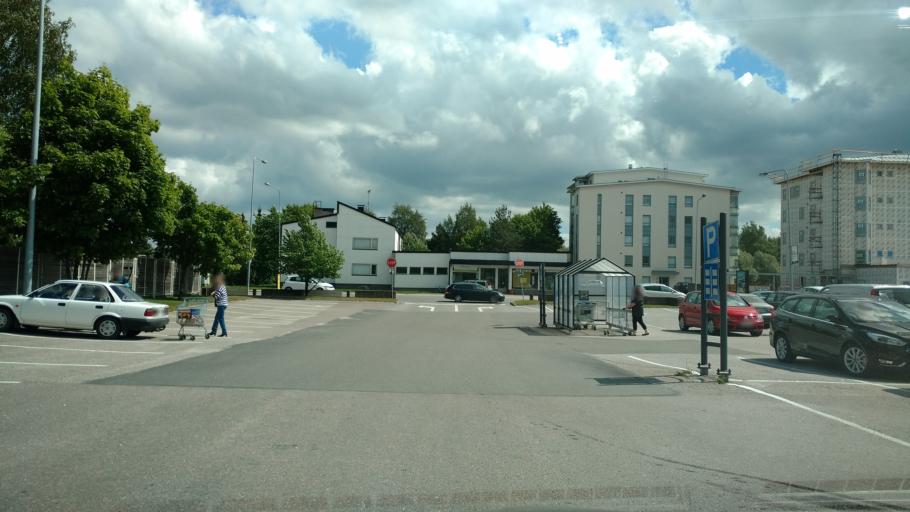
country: FI
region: Varsinais-Suomi
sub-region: Salo
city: Salo
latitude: 60.3911
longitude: 23.1271
